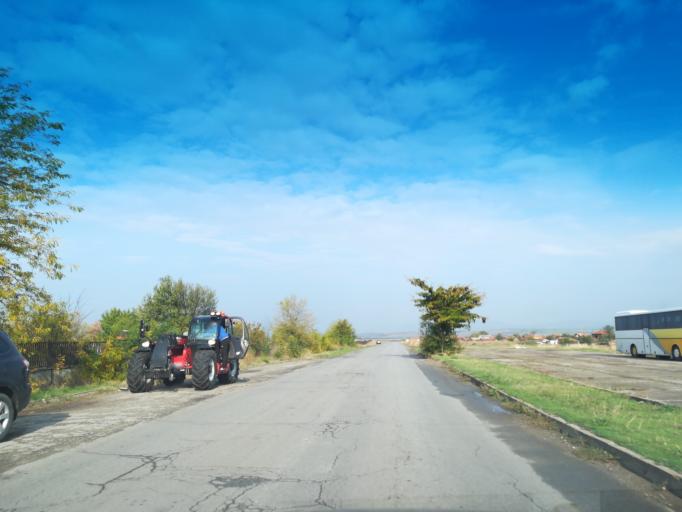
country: BG
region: Stara Zagora
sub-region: Obshtina Chirpan
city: Chirpan
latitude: 42.1970
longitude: 25.3118
